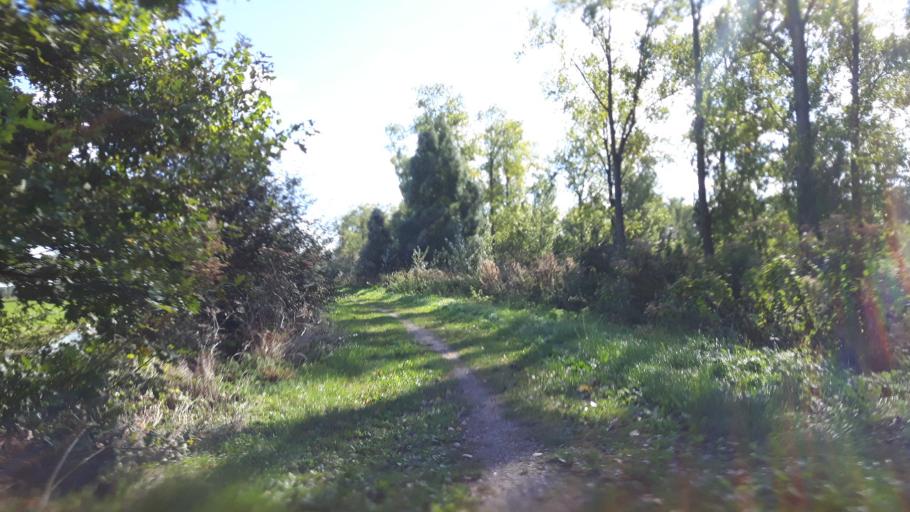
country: NL
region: Gelderland
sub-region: Gemeente Culemborg
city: Culemborg
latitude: 51.9343
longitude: 5.2598
